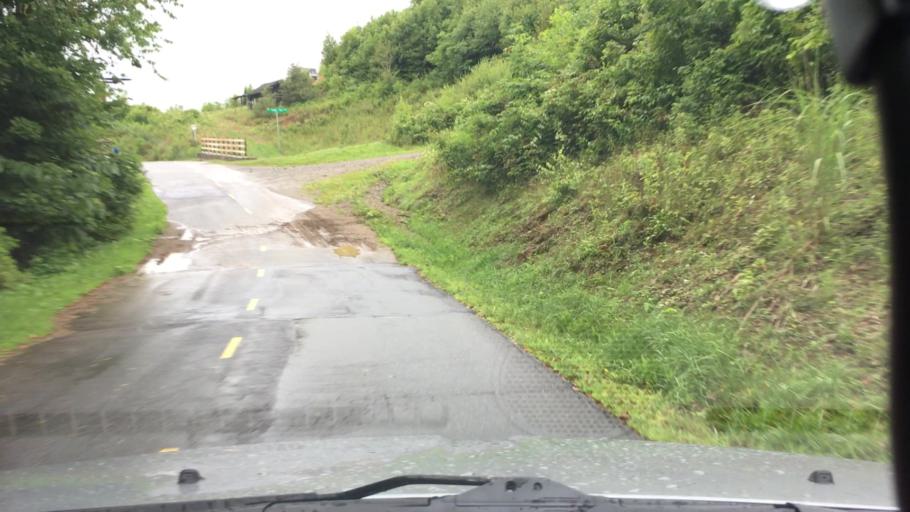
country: US
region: North Carolina
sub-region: Madison County
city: Mars Hill
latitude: 35.9464
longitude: -82.5114
